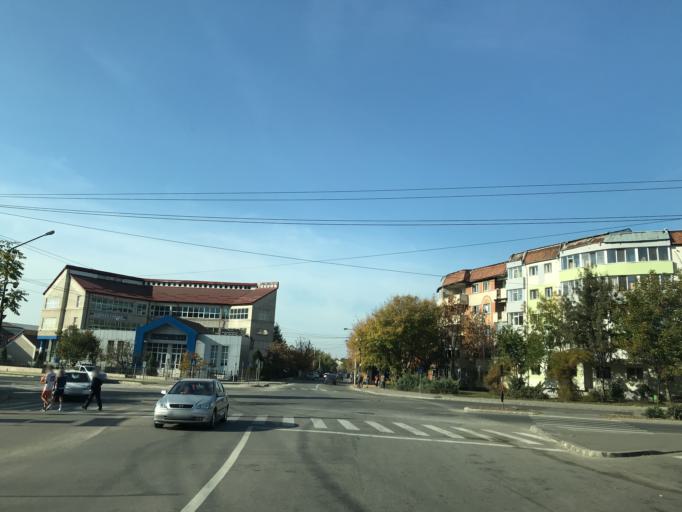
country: RO
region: Olt
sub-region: Municipiul Slatina
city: Slatina
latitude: 44.4310
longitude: 24.3537
